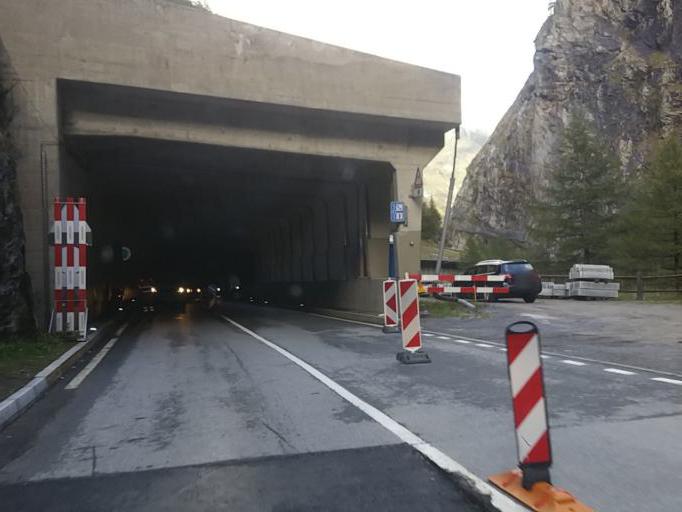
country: IT
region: Piedmont
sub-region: Provincia Verbano-Cusio-Ossola
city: Trasquera
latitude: 46.1874
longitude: 8.0948
